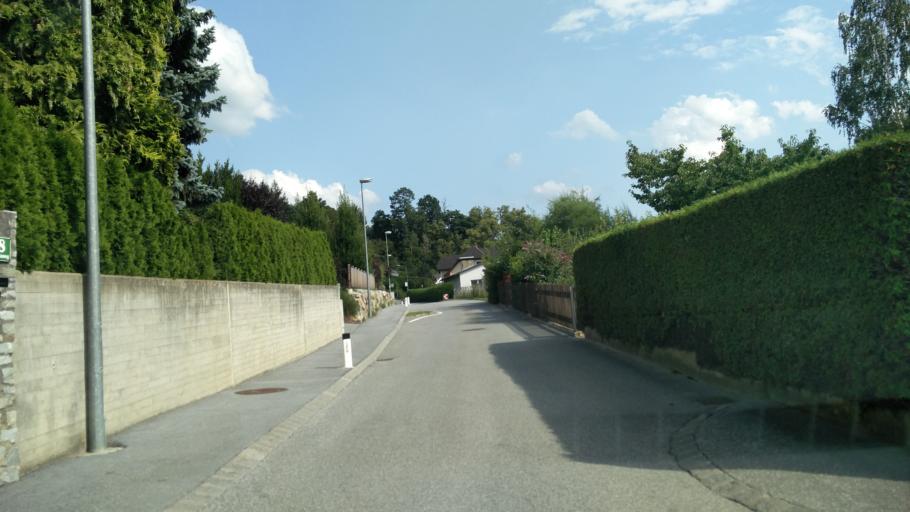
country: AT
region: Styria
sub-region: Politischer Bezirk Weiz
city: Weiz
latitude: 47.2241
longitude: 15.6294
